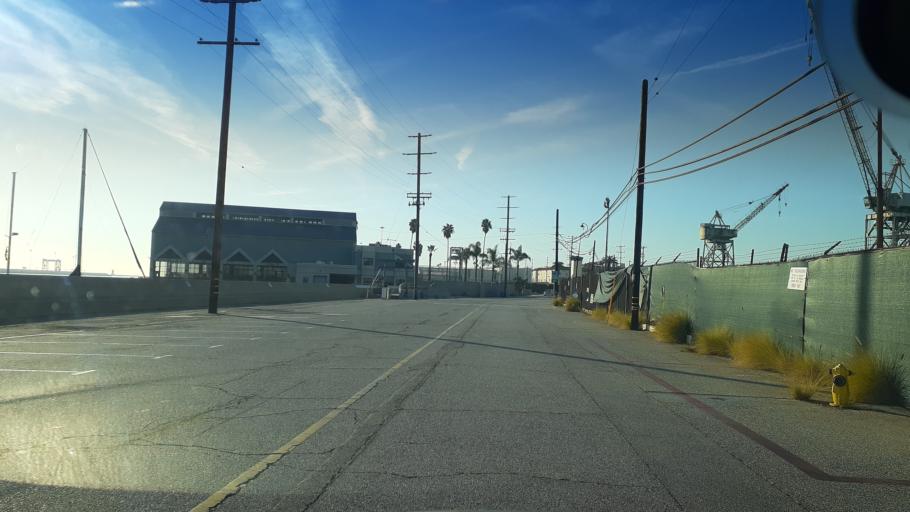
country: US
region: California
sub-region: Los Angeles County
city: San Pedro
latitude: 33.7314
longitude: -118.2685
